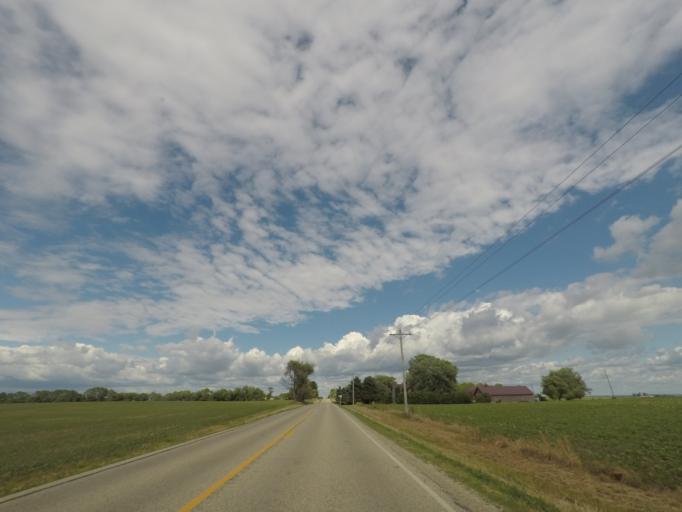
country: US
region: Wisconsin
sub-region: Rock County
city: Janesville
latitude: 42.7012
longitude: -89.1163
